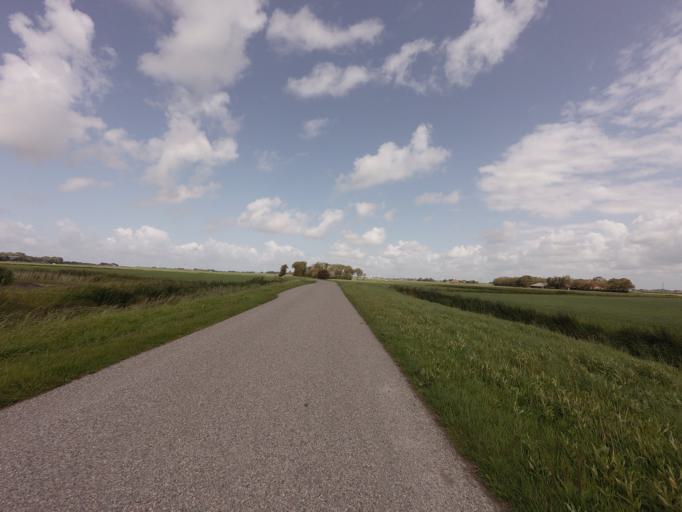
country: NL
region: Friesland
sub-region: Gemeente Franekeradeel
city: Sexbierum
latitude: 53.1585
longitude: 5.4824
